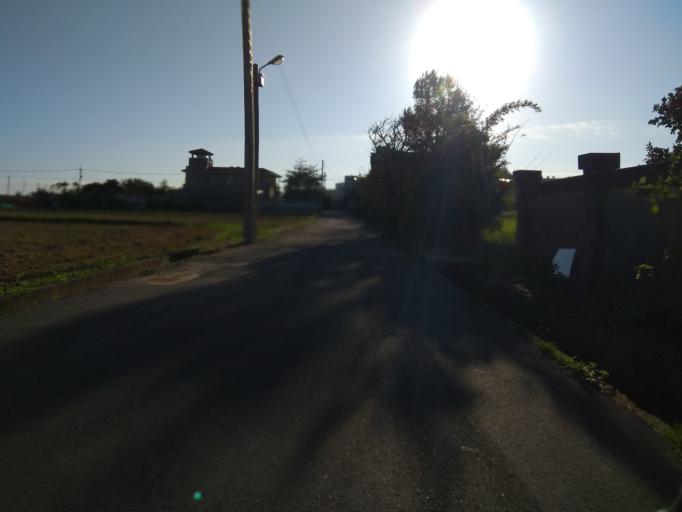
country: TW
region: Taiwan
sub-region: Hsinchu
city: Zhubei
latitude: 24.9889
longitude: 121.0446
